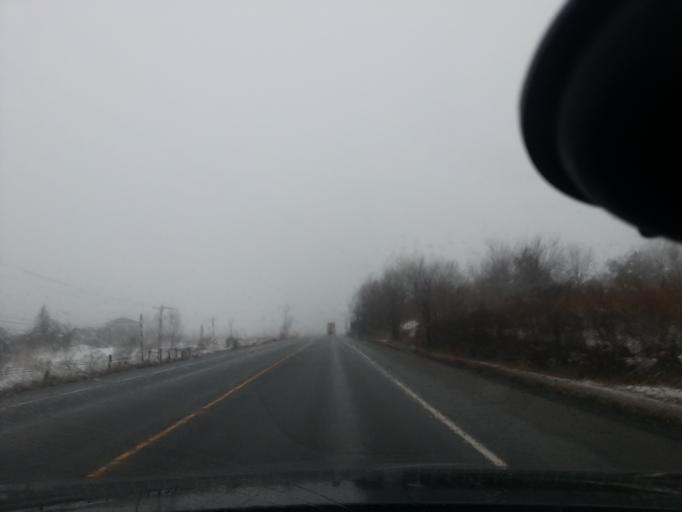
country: US
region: New York
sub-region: St. Lawrence County
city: Gouverneur
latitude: 44.3032
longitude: -75.5127
